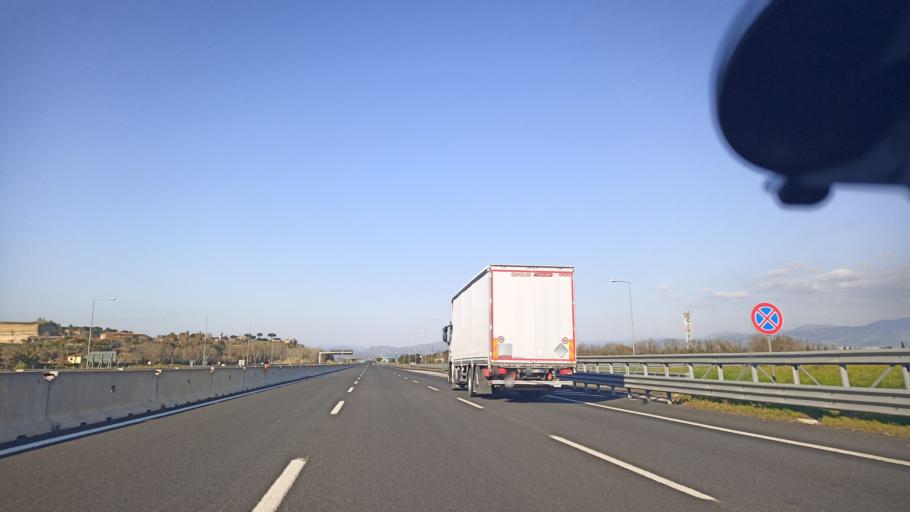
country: IT
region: Latium
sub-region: Citta metropolitana di Roma Capitale
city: Girardi-Bellavista-Terrazze
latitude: 42.0919
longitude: 12.5711
